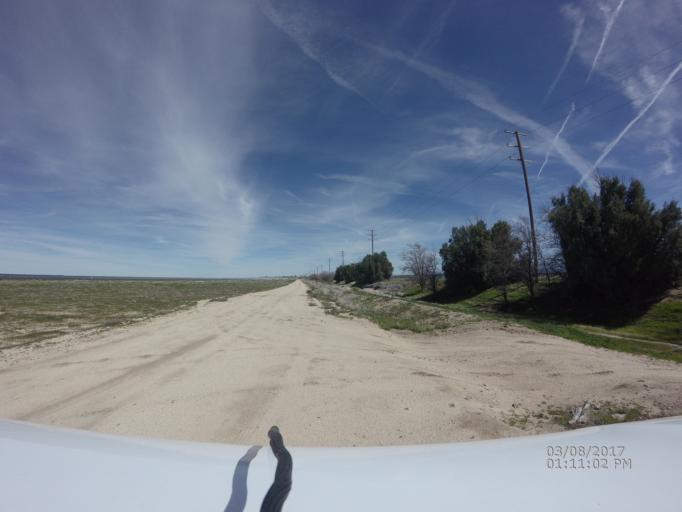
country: US
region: California
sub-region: Los Angeles County
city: Leona Valley
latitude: 34.7184
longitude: -118.3063
